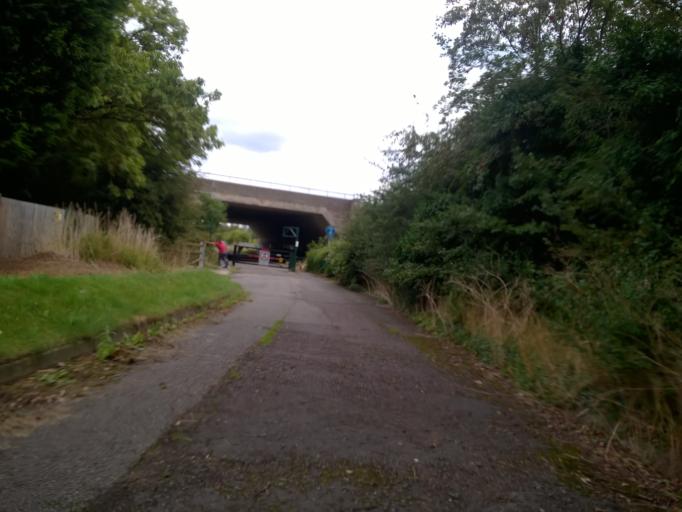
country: GB
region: England
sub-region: Leicestershire
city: Kirby Muxloe
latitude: 52.6409
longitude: -1.2240
